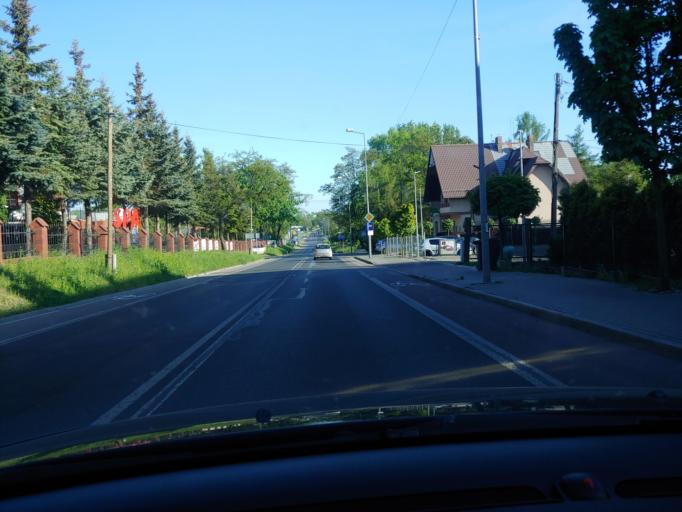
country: PL
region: Silesian Voivodeship
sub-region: Jaworzno
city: Jaworzno
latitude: 50.1964
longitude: 19.2816
